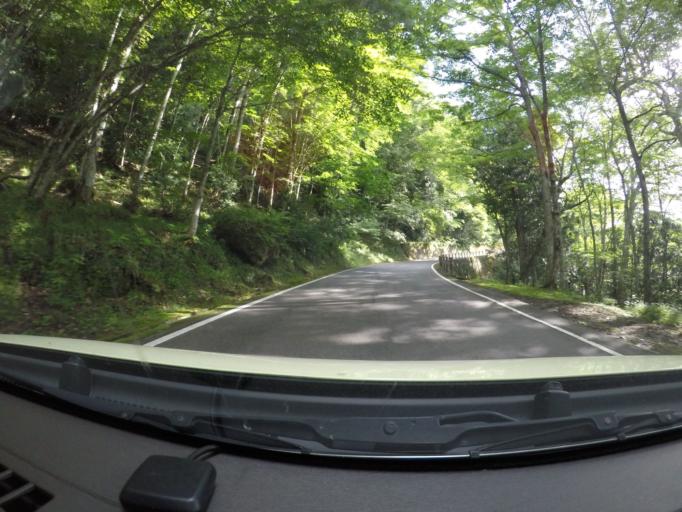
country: JP
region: Tochigi
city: Nikko
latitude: 36.8239
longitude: 139.3490
